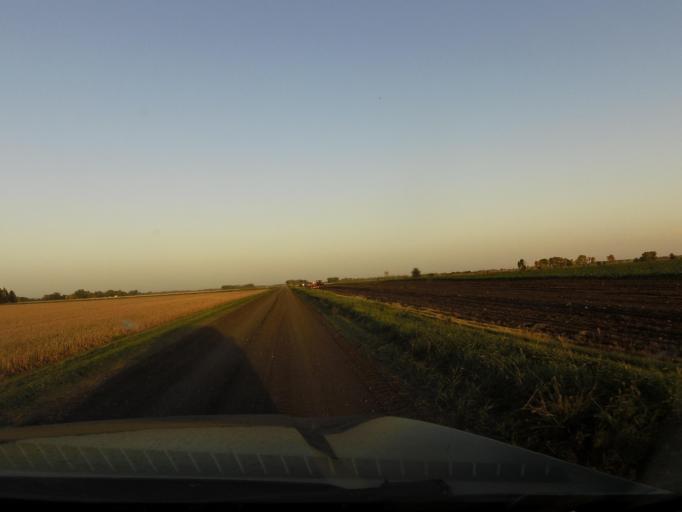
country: US
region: North Dakota
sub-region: Walsh County
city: Grafton
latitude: 48.3832
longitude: -97.2281
